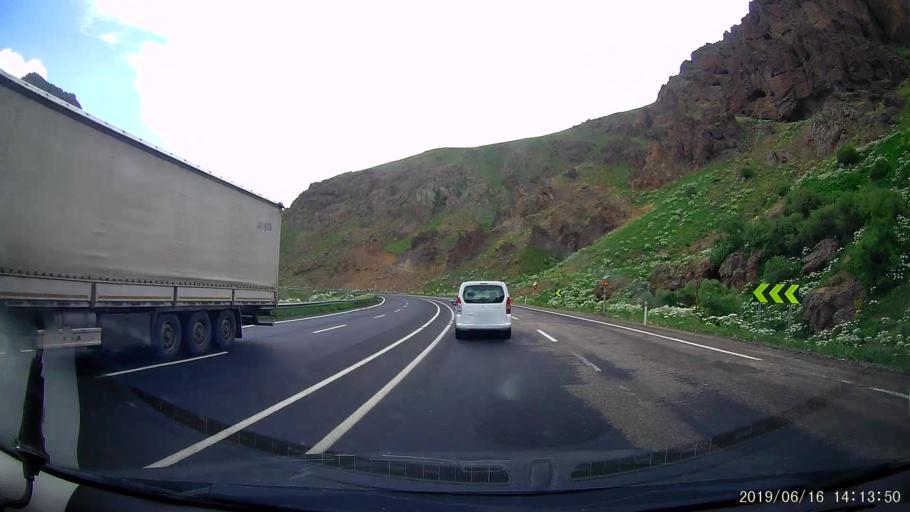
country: TR
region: Agri
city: Tahir
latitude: 39.7962
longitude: 42.5084
